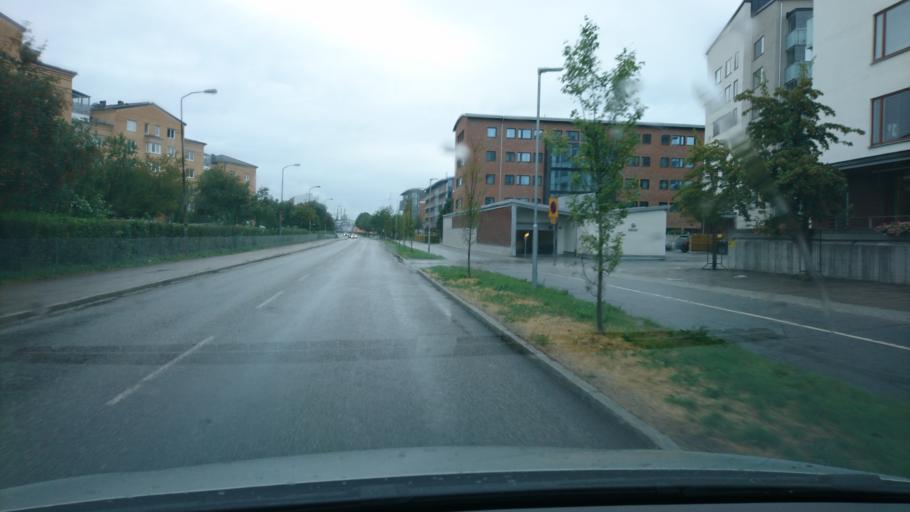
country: SE
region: Uppsala
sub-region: Uppsala Kommun
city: Uppsala
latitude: 59.8696
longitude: 17.6175
